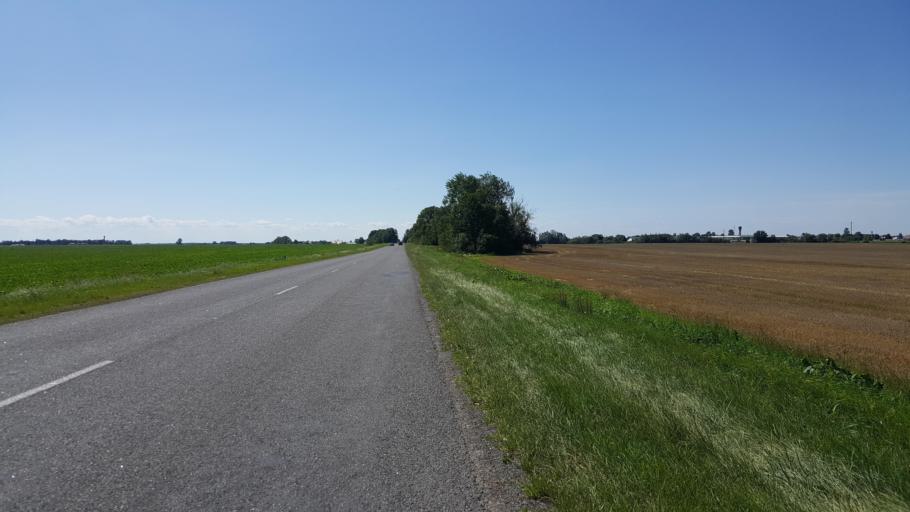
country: BY
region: Brest
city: Charnawchytsy
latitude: 52.2055
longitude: 23.7791
